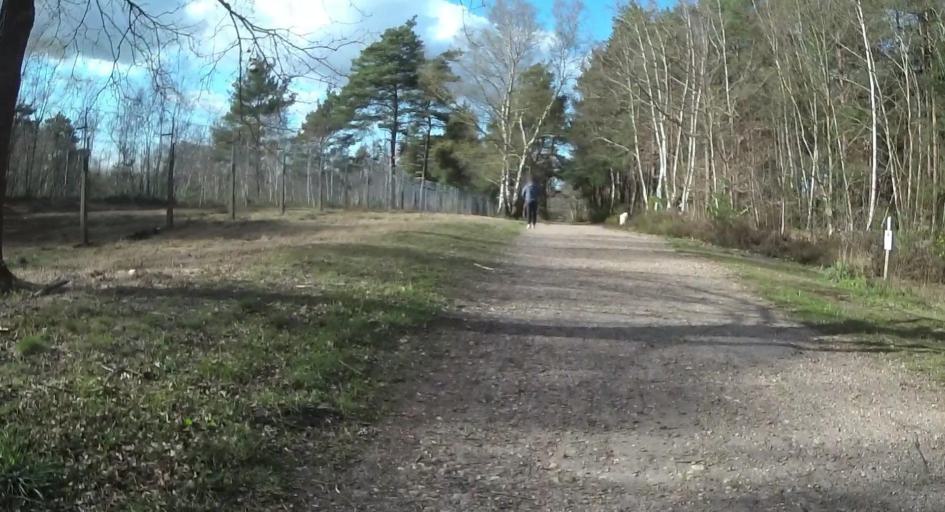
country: GB
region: England
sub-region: Surrey
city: Windlesham
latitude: 51.3419
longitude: -0.6649
